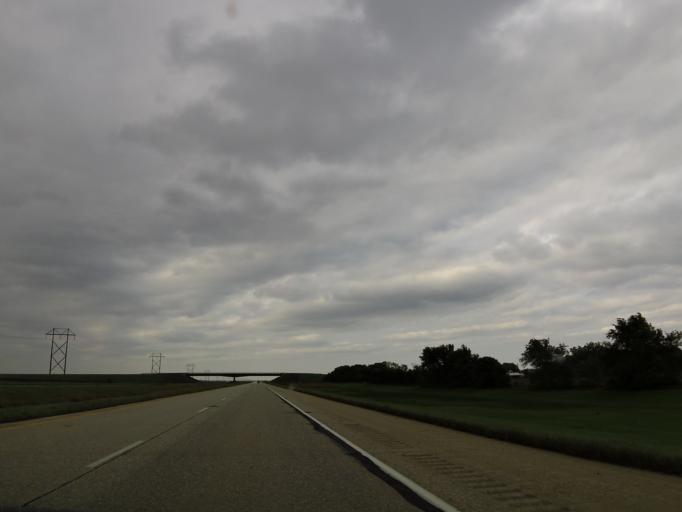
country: US
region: North Dakota
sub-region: Richland County
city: Wahpeton
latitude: 46.1786
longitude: -96.8338
